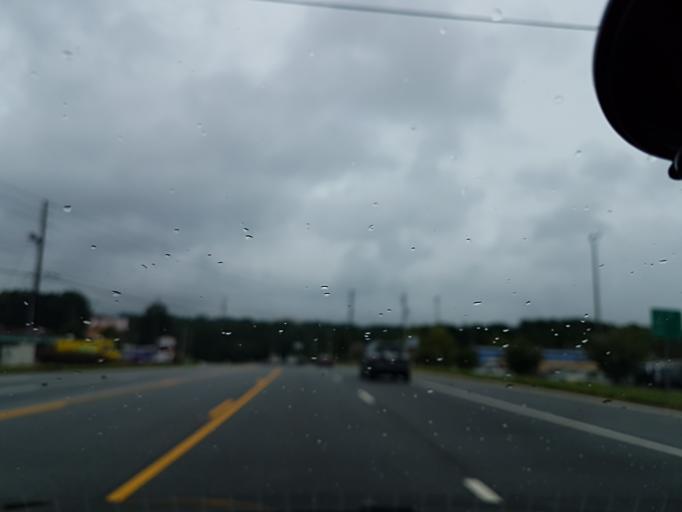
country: US
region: Georgia
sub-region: Gwinnett County
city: Norcross
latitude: 33.9460
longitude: -84.2407
